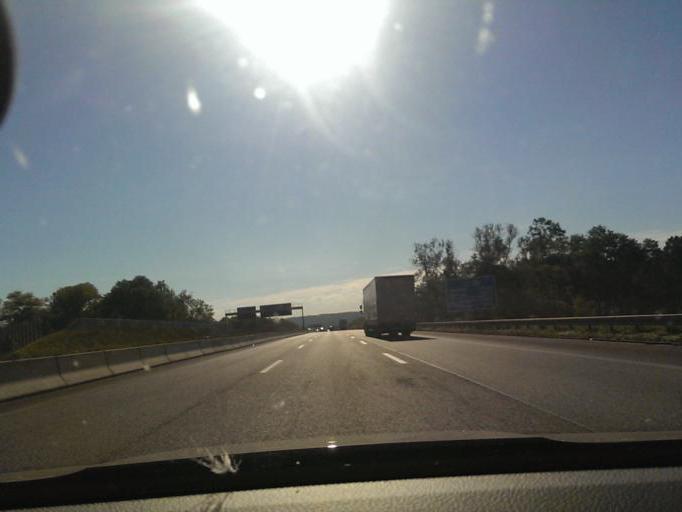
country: DE
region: Baden-Wuerttemberg
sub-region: Regierungsbezirk Stuttgart
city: Rutesheim
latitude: 48.8104
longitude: 8.9227
